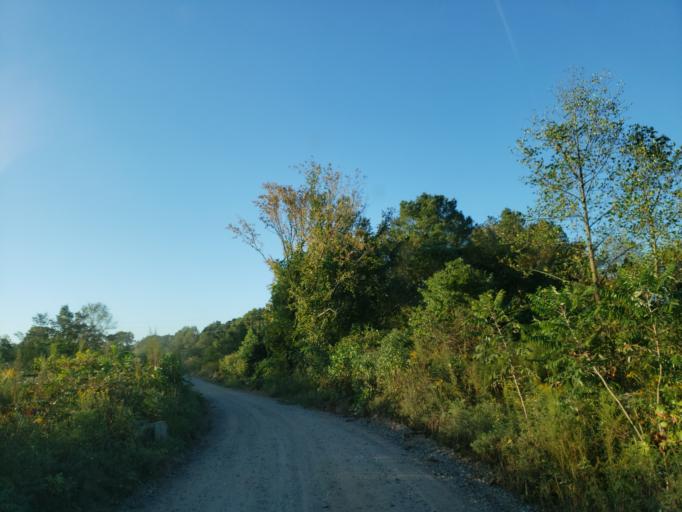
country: US
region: Georgia
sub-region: Pickens County
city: Jasper
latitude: 34.4518
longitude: -84.4442
